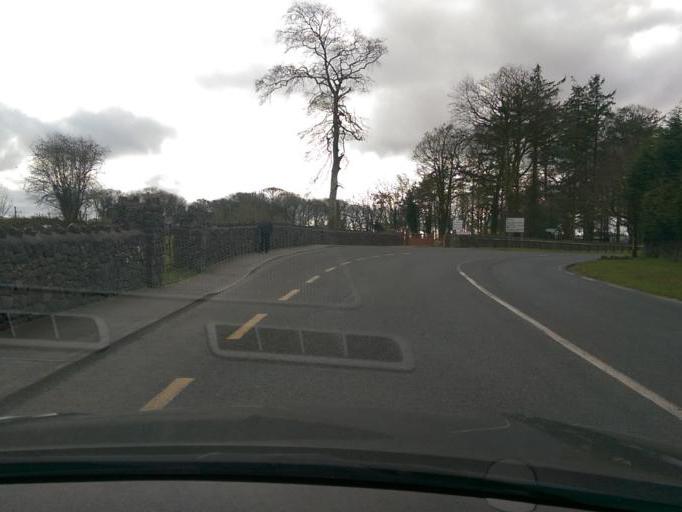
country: IE
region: Connaught
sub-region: County Galway
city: Ballinasloe
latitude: 53.3290
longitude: -8.4051
